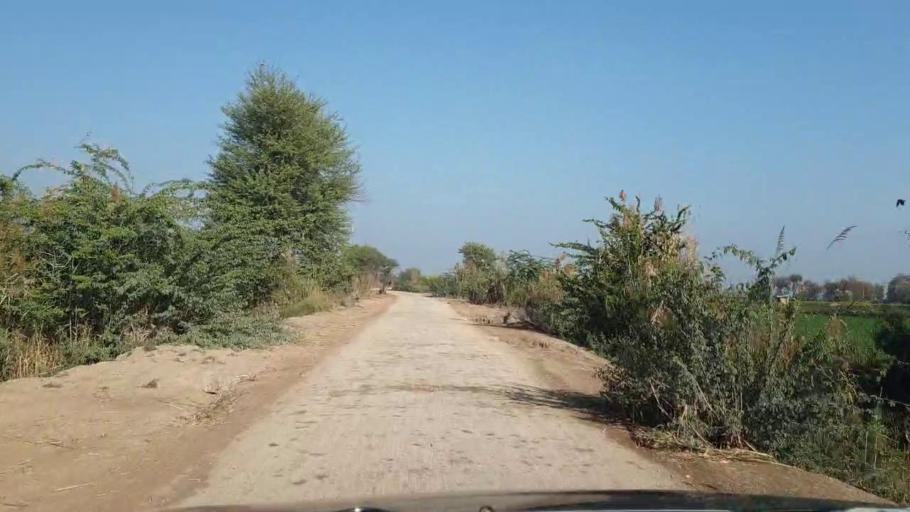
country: PK
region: Sindh
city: Sinjhoro
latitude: 26.0621
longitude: 68.7880
